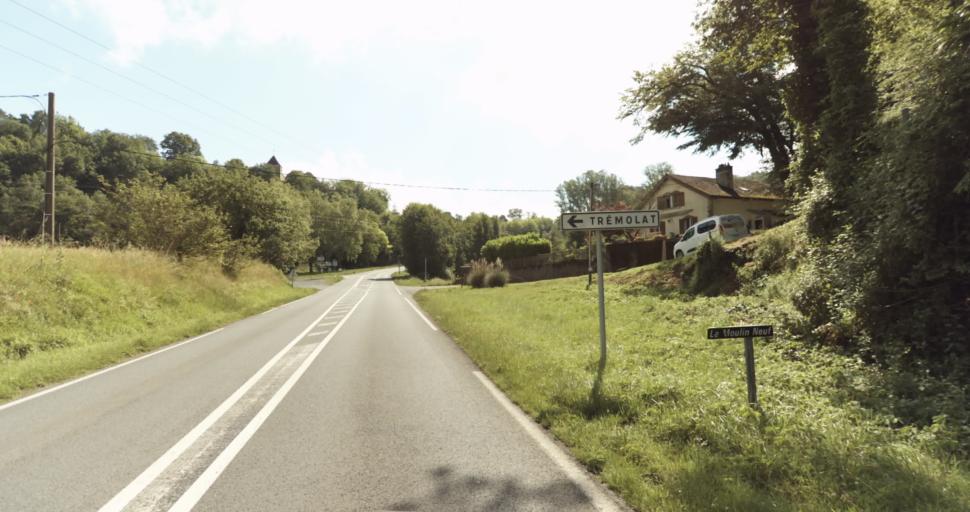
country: FR
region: Aquitaine
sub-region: Departement de la Dordogne
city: Lalinde
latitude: 44.8539
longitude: 0.8077
